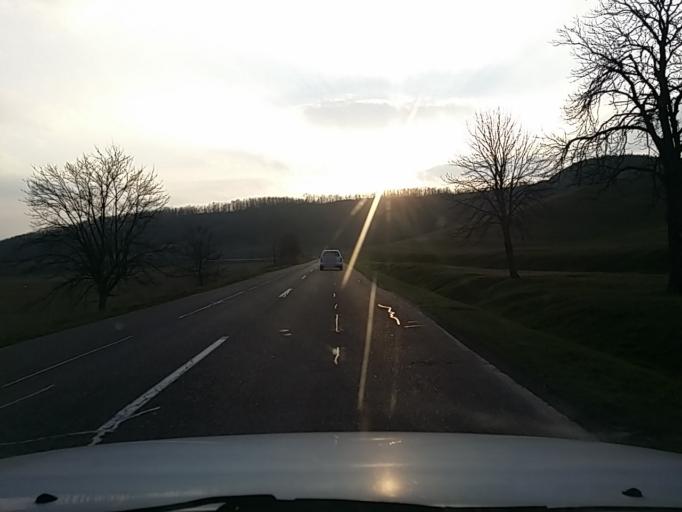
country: HU
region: Heves
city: Petervasara
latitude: 48.0428
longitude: 20.1329
